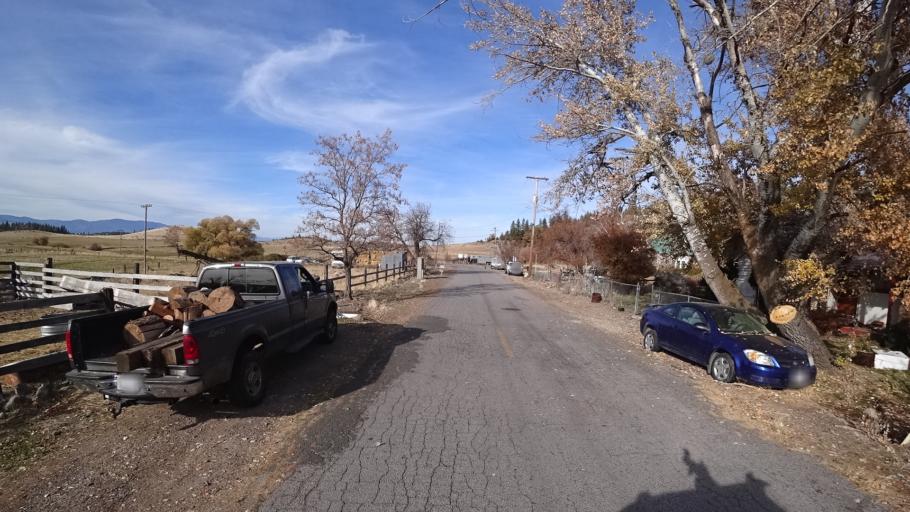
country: US
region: California
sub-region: Siskiyou County
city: Weed
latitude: 41.4643
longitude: -122.3871
